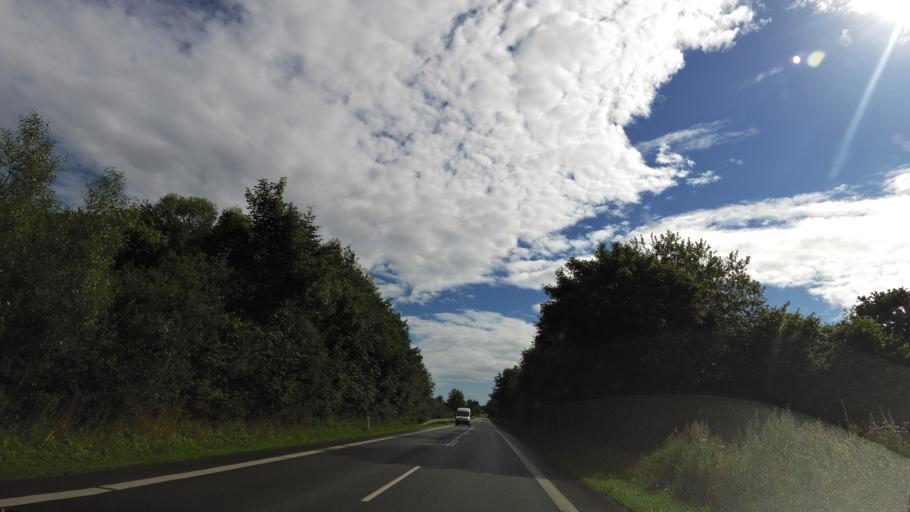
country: DK
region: South Denmark
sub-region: Assens Kommune
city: Vissenbjerg
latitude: 55.4187
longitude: 10.1769
